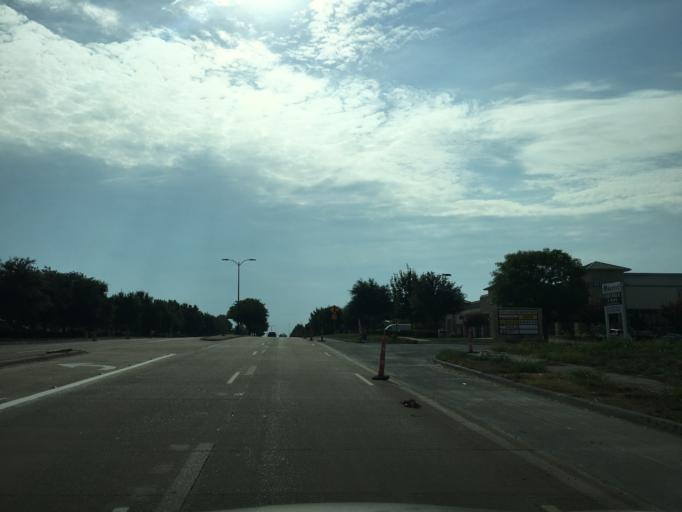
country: US
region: Texas
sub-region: Collin County
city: McKinney
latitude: 33.1988
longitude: -96.6526
